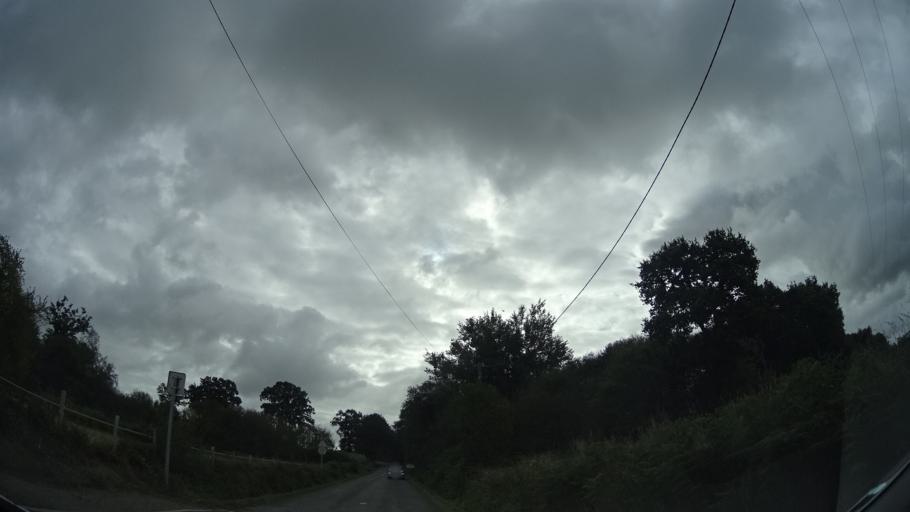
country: FR
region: Brittany
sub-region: Departement d'Ille-et-Vilaine
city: Montreuil-sur-Ille
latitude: 48.3032
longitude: -1.6612
